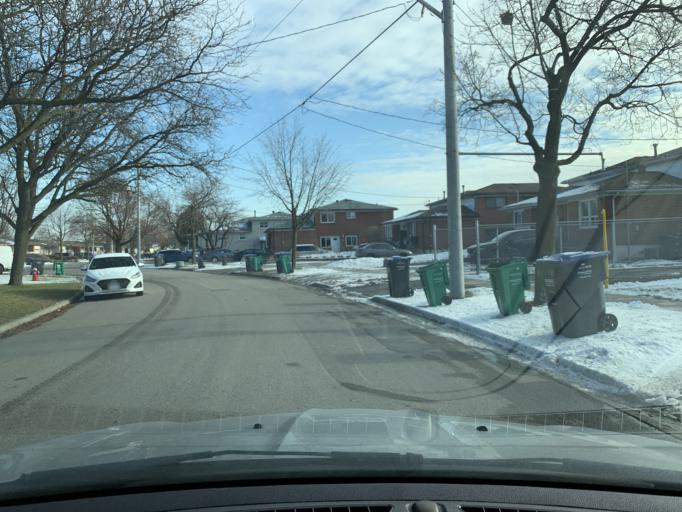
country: CA
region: Ontario
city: Etobicoke
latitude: 43.7240
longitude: -79.6307
